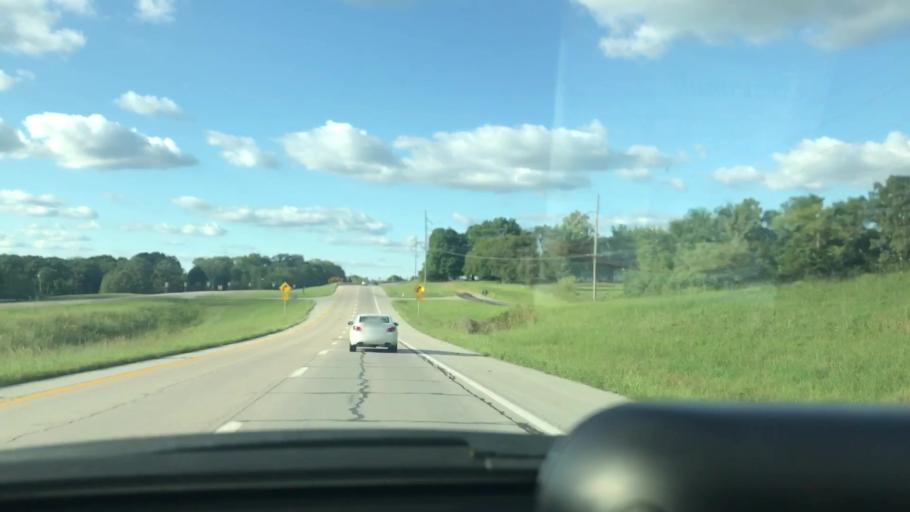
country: US
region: Missouri
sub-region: Pettis County
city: Sedalia
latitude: 38.6323
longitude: -93.2672
